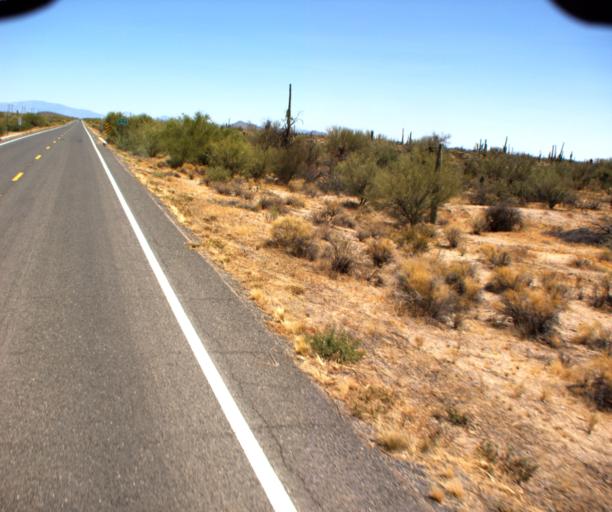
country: US
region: Arizona
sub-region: Pinal County
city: Florence
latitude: 32.8202
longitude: -111.2018
